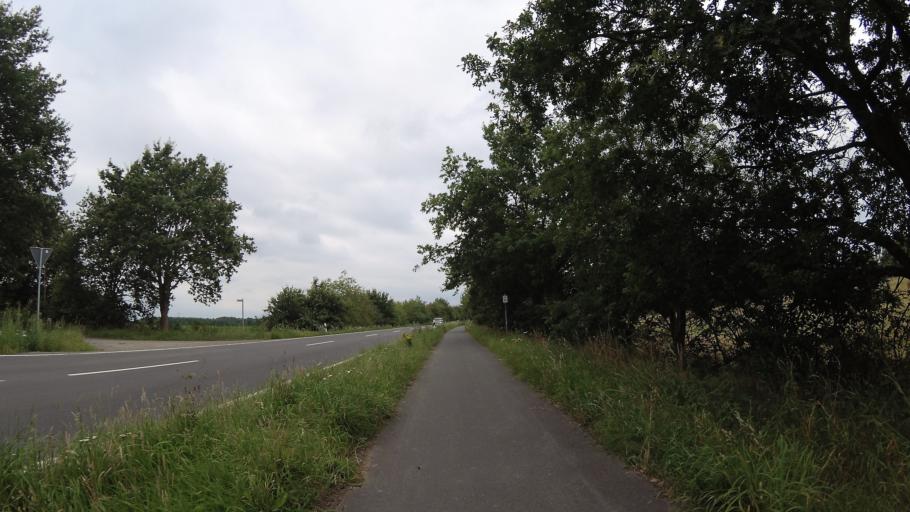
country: DE
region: Lower Saxony
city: Oberlangen
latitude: 52.8349
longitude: 7.2546
